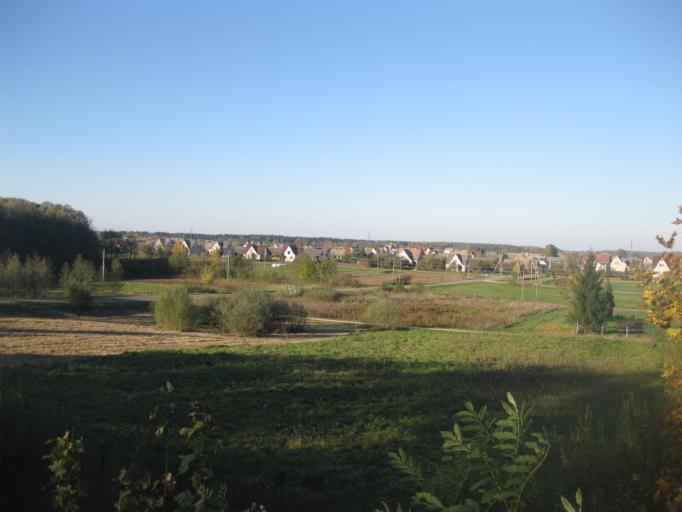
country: LT
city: Vilkija
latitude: 55.0419
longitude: 23.5914
